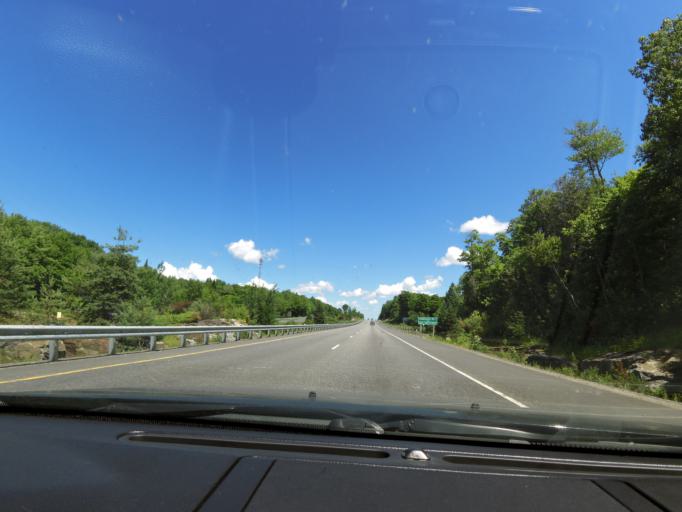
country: CA
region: Ontario
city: Bracebridge
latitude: 45.1492
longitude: -79.3111
